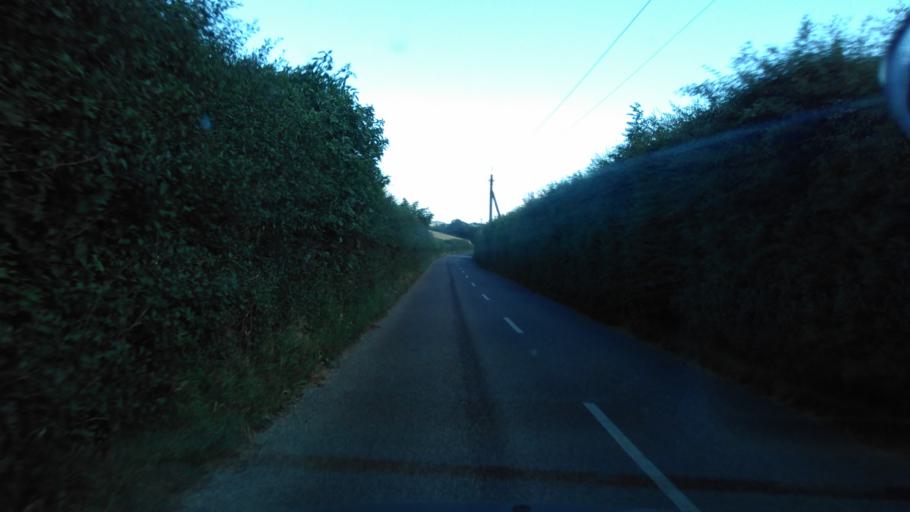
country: GB
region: England
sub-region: Kent
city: Dunkirk
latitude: 51.2585
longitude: 0.9553
